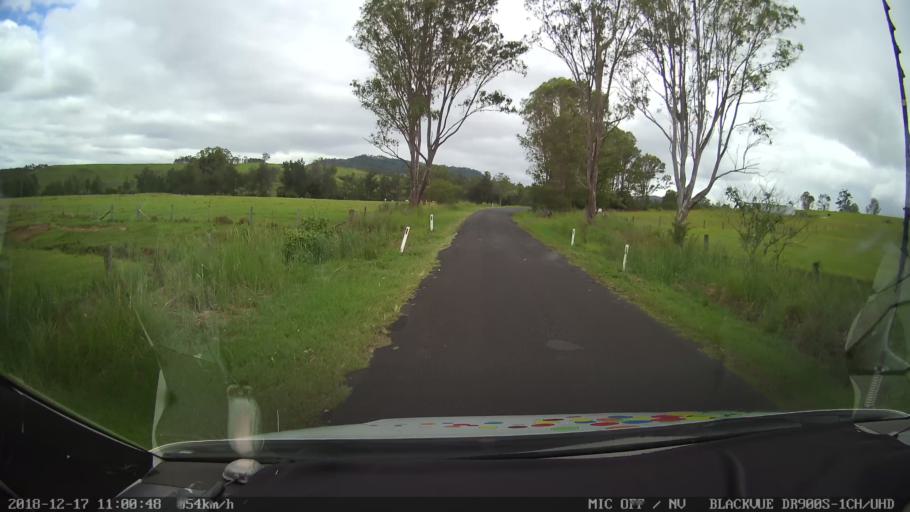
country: AU
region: New South Wales
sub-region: Richmond Valley
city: Casino
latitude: -28.8180
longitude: 152.6210
